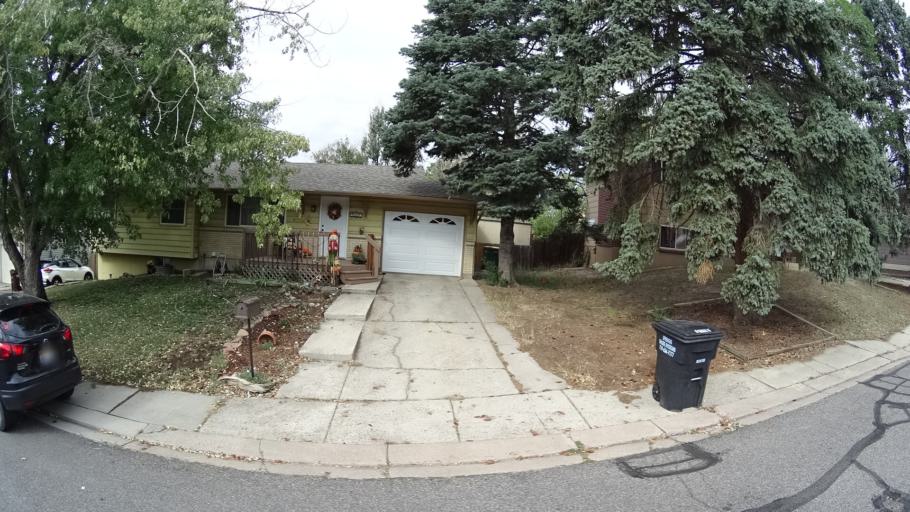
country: US
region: Colorado
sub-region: El Paso County
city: Cimarron Hills
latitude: 38.8555
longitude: -104.7421
